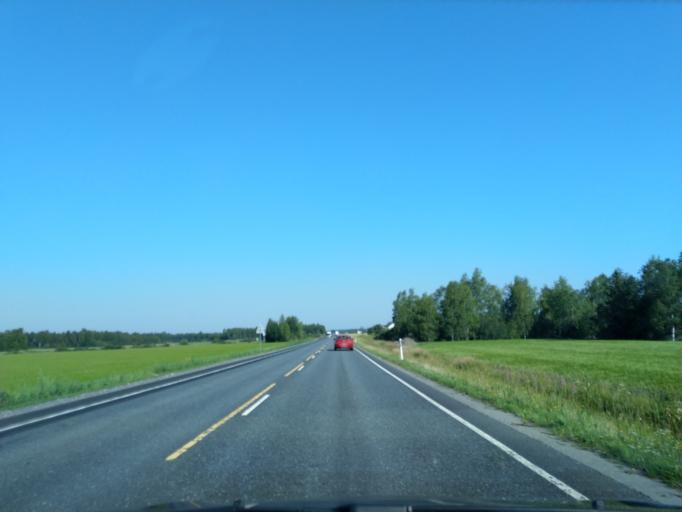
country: FI
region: Haeme
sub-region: Forssa
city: Tammela
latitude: 60.7536
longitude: 23.7083
